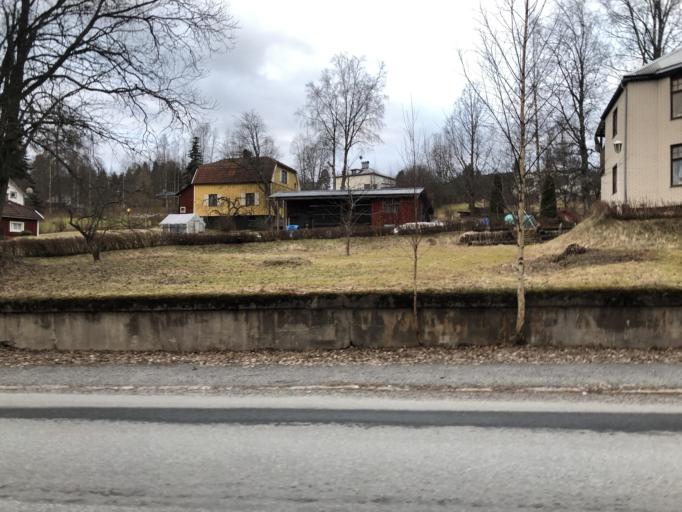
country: SE
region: Vaermland
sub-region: Filipstads Kommun
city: Lesjofors
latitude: 59.9768
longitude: 14.1814
